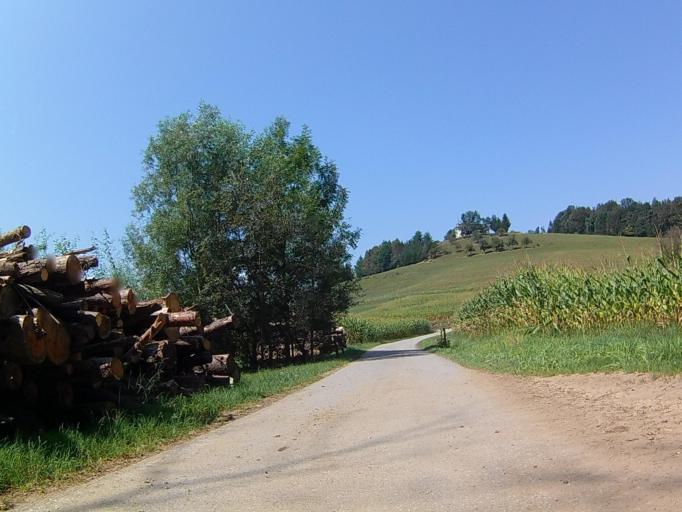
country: AT
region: Styria
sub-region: Politischer Bezirk Deutschlandsberg
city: Pitschgau
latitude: 46.7036
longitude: 15.2936
